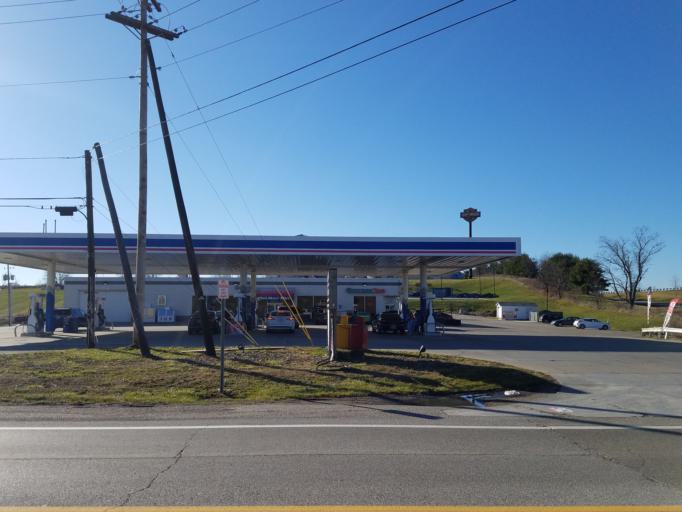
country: US
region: Ohio
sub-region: Belmont County
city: Bethesda
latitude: 40.0588
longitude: -81.0523
